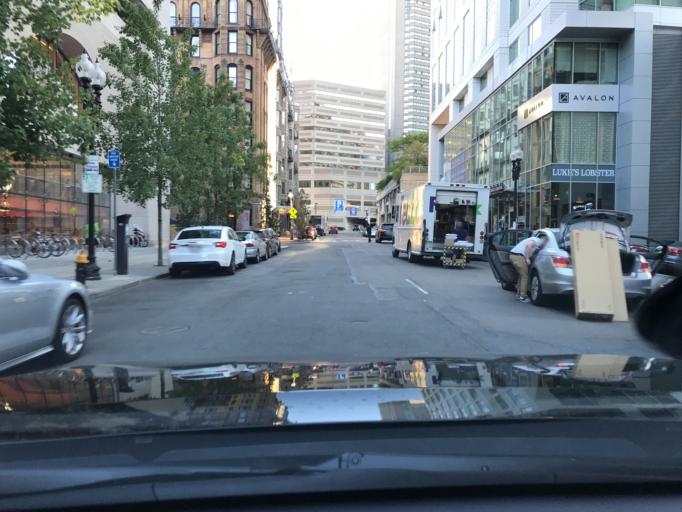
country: US
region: Massachusetts
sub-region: Suffolk County
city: Boston
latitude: 42.3491
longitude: -71.0793
